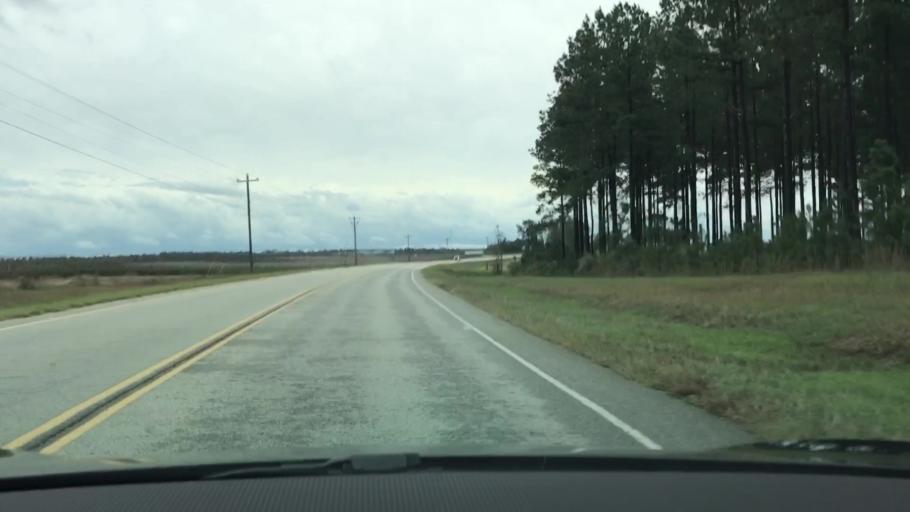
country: US
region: Georgia
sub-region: Jefferson County
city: Wrens
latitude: 33.1128
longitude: -82.4308
